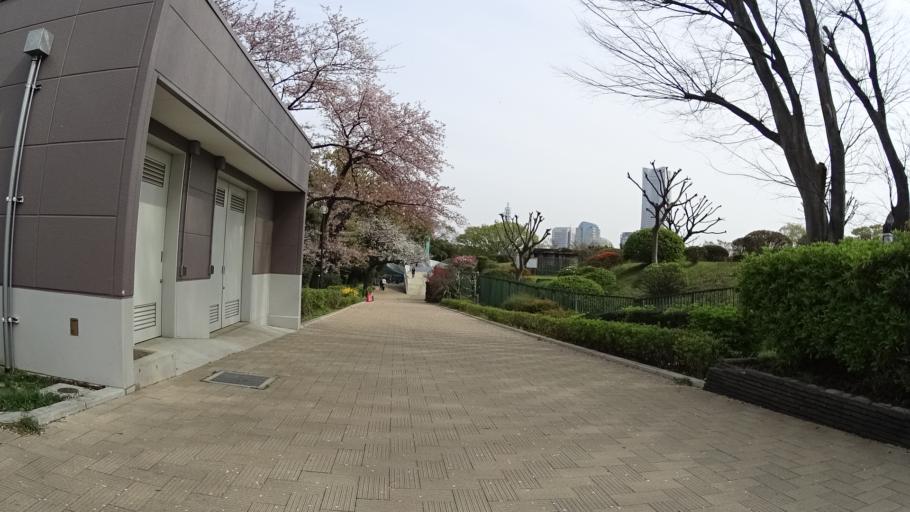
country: JP
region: Kanagawa
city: Yokohama
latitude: 35.4454
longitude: 139.6227
